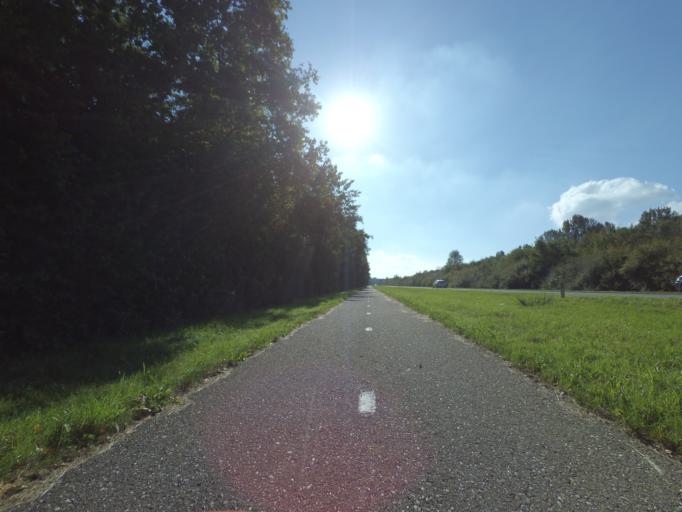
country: NL
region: Flevoland
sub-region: Gemeente Zeewolde
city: Zeewolde
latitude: 52.2989
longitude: 5.5119
